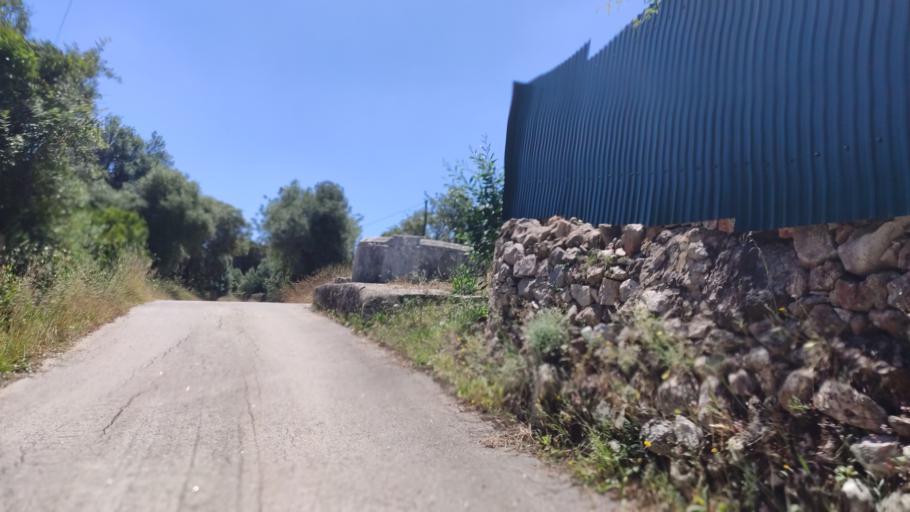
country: PT
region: Faro
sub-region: Sao Bras de Alportel
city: Sao Bras de Alportel
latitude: 37.1713
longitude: -7.9130
